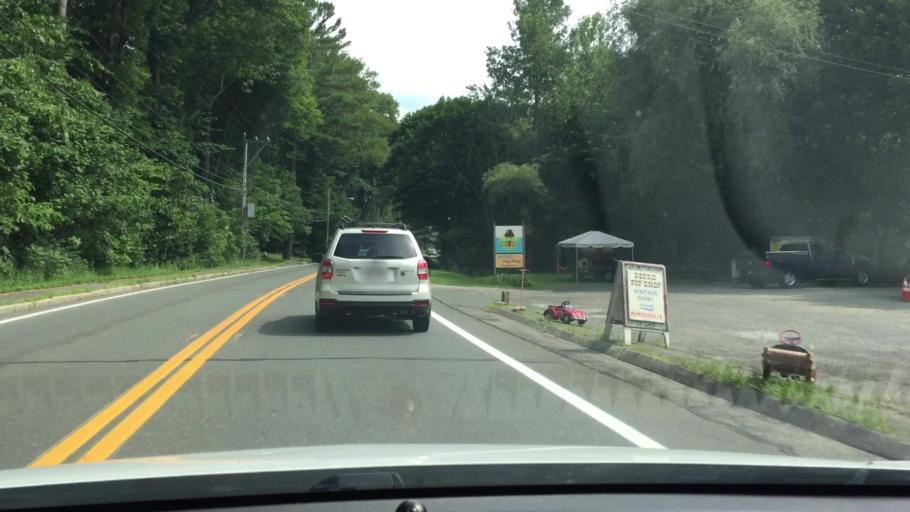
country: US
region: Massachusetts
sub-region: Berkshire County
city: Lee
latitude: 42.3209
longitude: -73.2587
